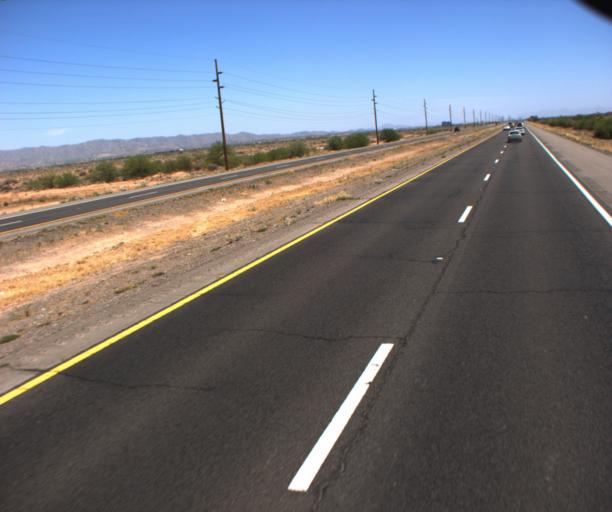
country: US
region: Arizona
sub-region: Maricopa County
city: Sun Lakes
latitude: 33.2359
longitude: -111.9832
